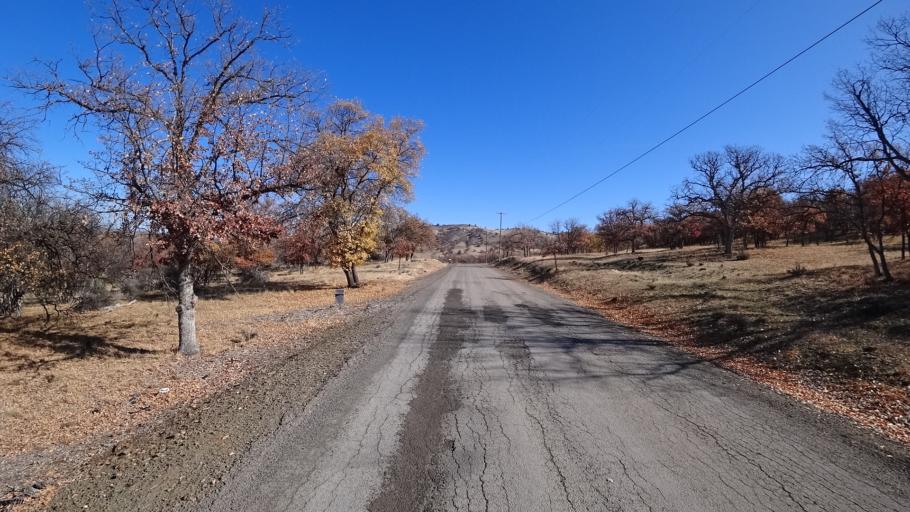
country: US
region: California
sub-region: Siskiyou County
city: Montague
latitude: 41.8846
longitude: -122.4876
